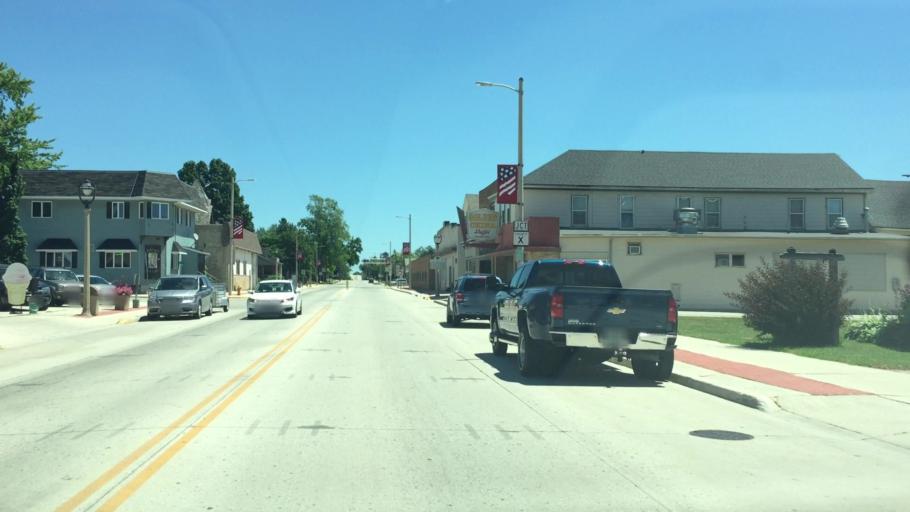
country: US
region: Wisconsin
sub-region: Calumet County
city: New Holstein
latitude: 43.9497
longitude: -88.0871
